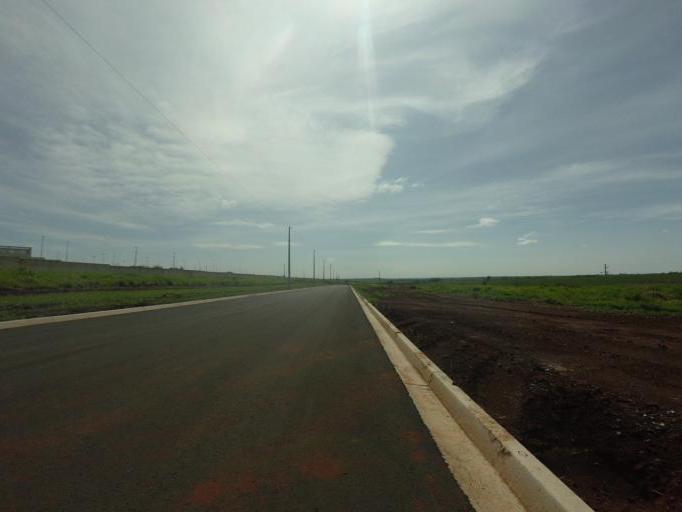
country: BR
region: Sao Paulo
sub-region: Piracicaba
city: Piracicaba
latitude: -22.7634
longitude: -47.5830
